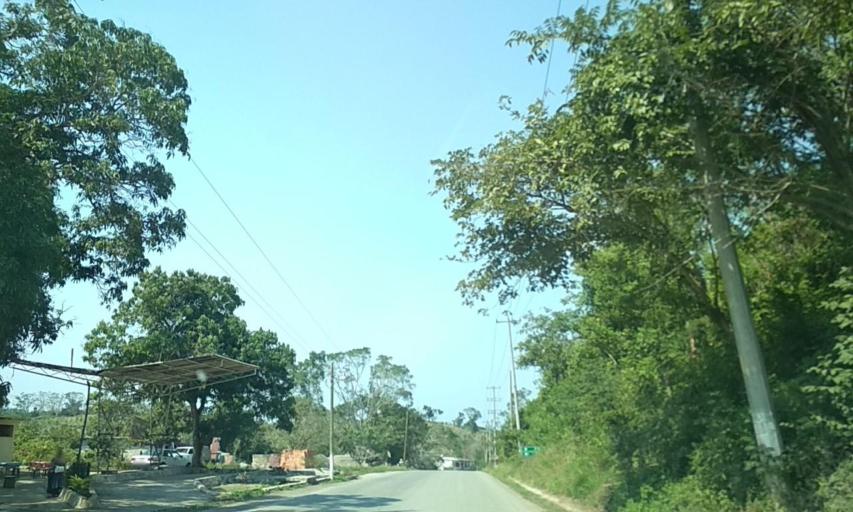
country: MX
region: Veracruz
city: Agua Dulce
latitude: 20.3724
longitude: -97.1808
